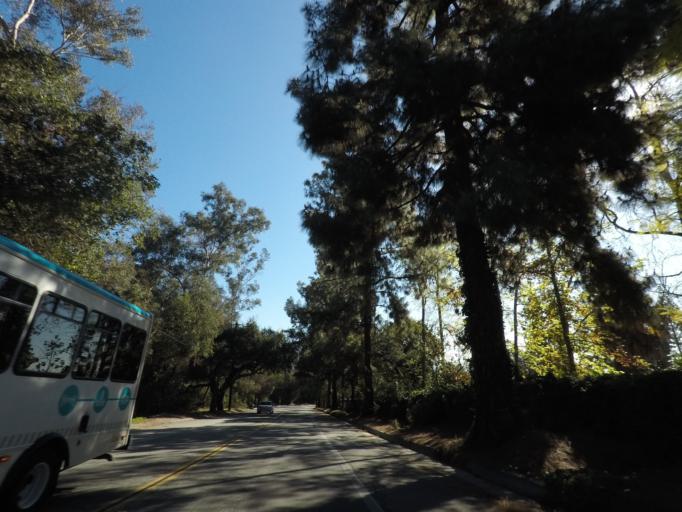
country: US
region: California
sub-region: Los Angeles County
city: La Canada Flintridge
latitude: 34.1726
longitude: -118.1873
